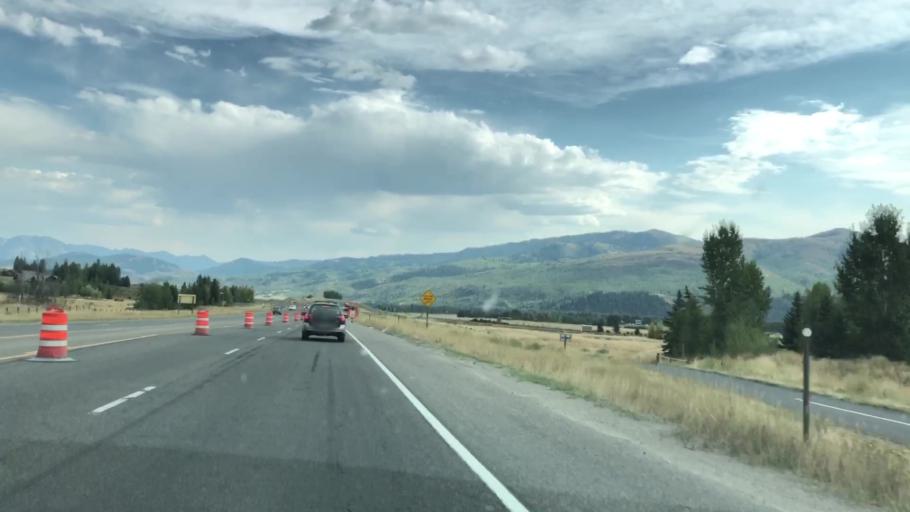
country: US
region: Wyoming
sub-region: Teton County
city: South Park
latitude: 43.4175
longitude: -110.7745
